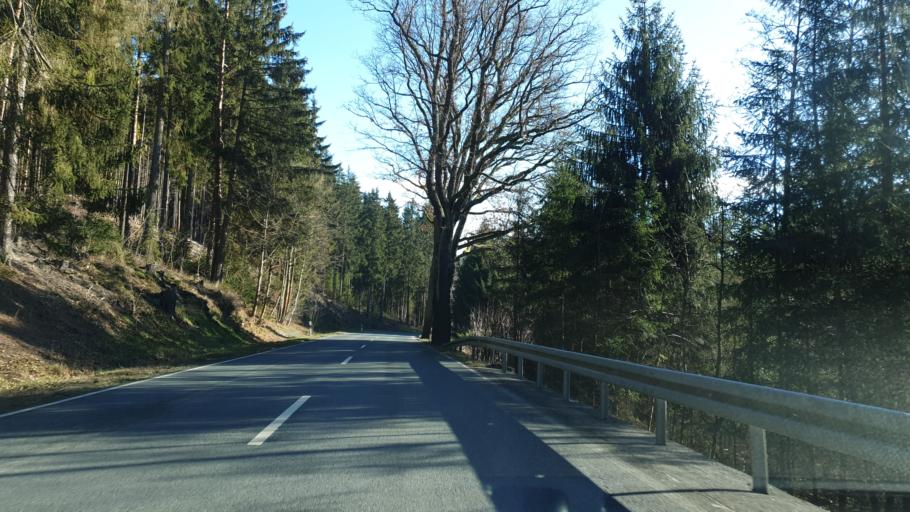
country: DE
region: Saxony
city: Adorf
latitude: 50.2776
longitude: 12.2895
